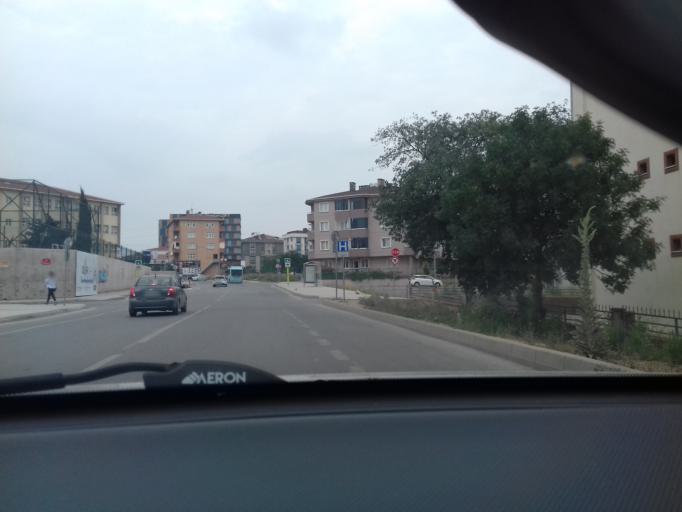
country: TR
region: Istanbul
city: Pendik
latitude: 40.9105
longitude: 29.2989
